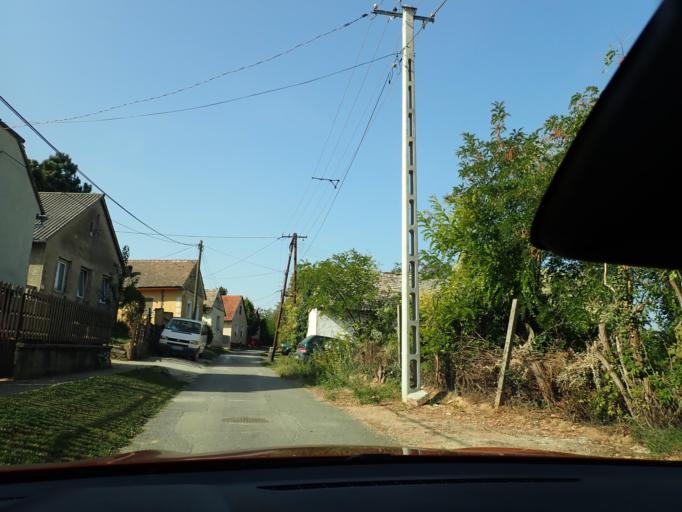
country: HU
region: Baranya
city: Boly
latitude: 45.9992
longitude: 18.5079
